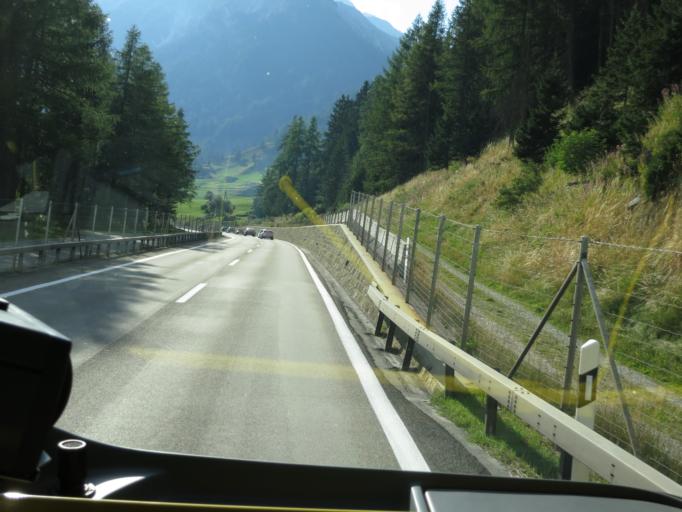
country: CH
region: Grisons
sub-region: Hinterrhein District
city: Thusis
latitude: 46.5710
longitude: 9.3798
